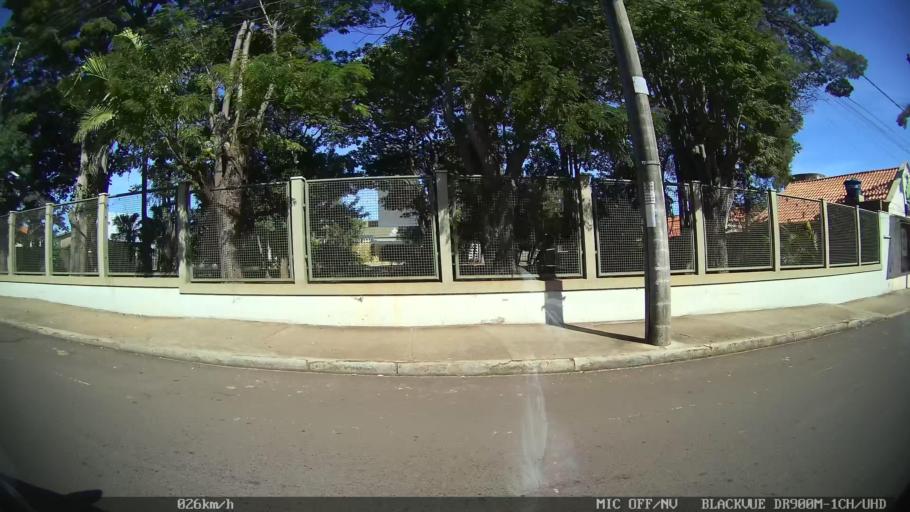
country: BR
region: Sao Paulo
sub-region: Franca
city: Franca
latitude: -20.5442
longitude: -47.3915
